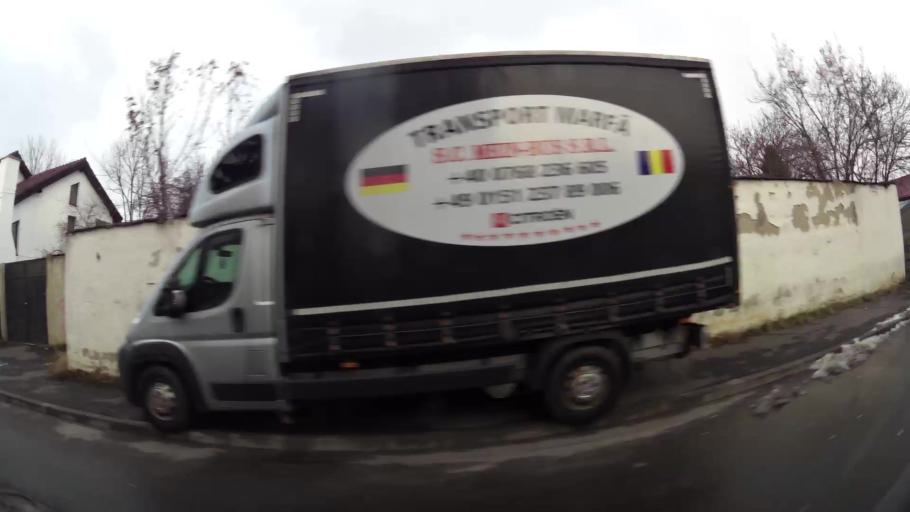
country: RO
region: Ilfov
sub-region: Comuna Fundeni-Dobroesti
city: Fundeni
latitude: 44.4719
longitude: 26.1626
